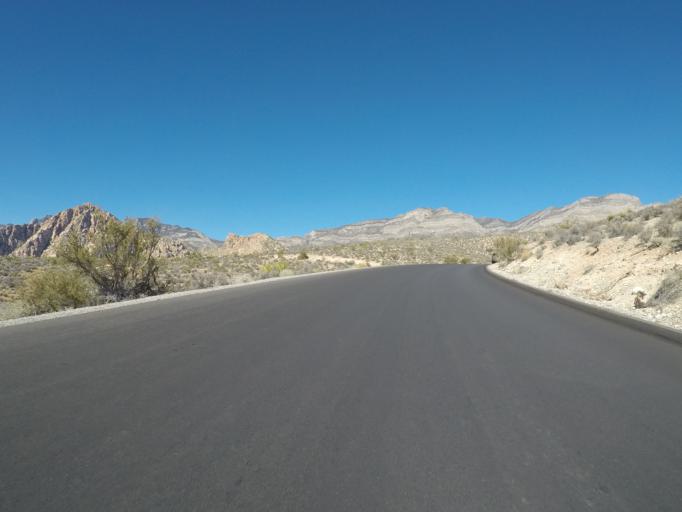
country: US
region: Nevada
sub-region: Clark County
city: Summerlin South
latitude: 36.1629
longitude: -115.4611
